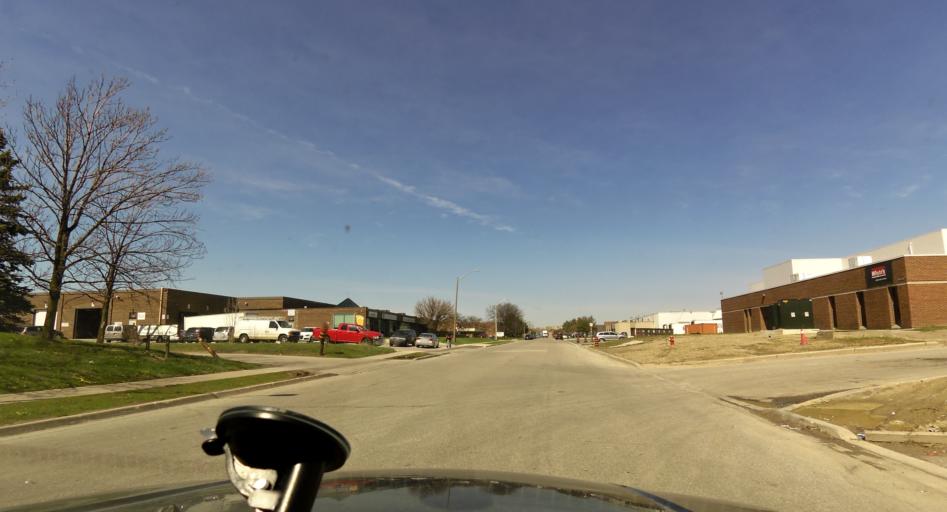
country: CA
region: Ontario
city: Etobicoke
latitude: 43.6420
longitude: -79.6215
